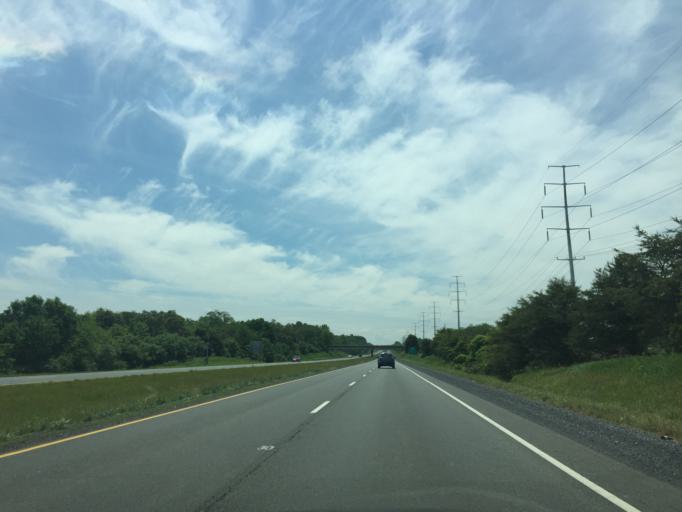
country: US
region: Virginia
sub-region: City of Winchester
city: Winchester
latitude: 39.1787
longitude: -78.2059
